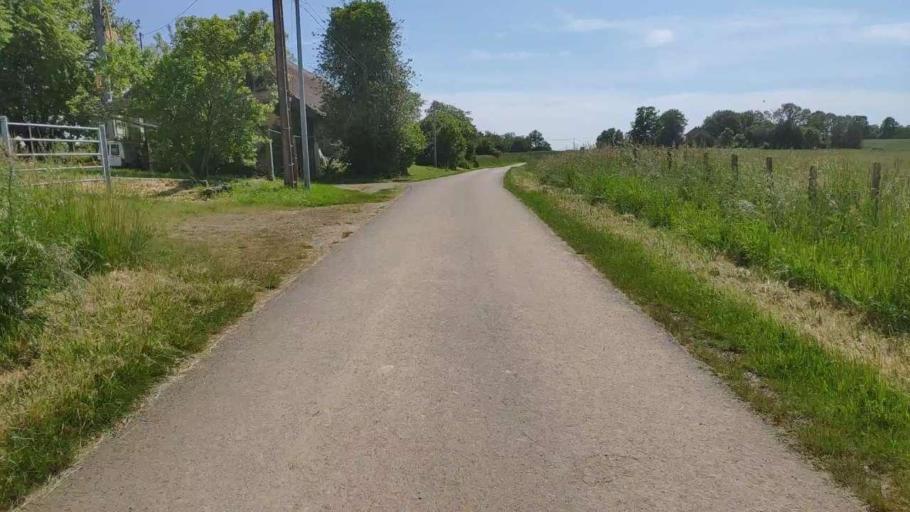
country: FR
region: Franche-Comte
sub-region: Departement du Jura
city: Bletterans
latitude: 46.7915
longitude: 5.4145
